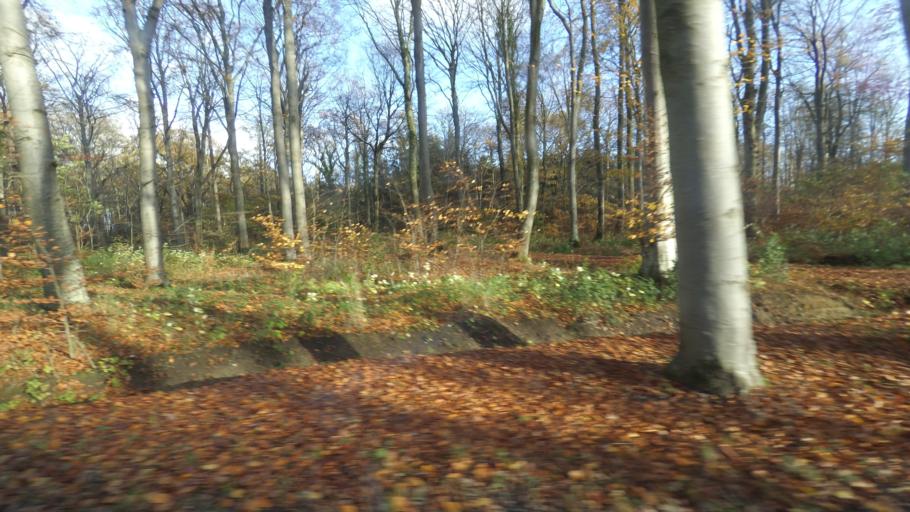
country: DK
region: Central Jutland
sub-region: Odder Kommune
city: Odder
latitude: 55.8582
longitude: 10.1620
